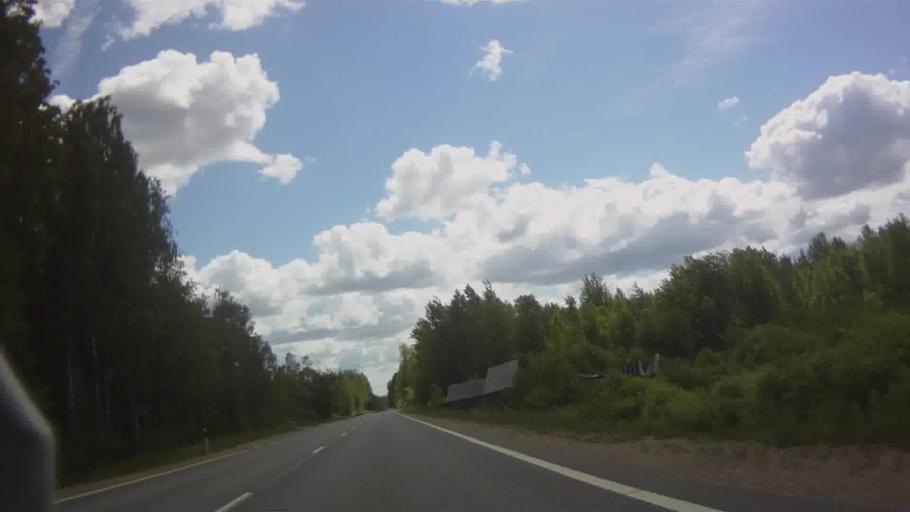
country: LV
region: Livani
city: Livani
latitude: 56.5431
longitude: 26.1235
